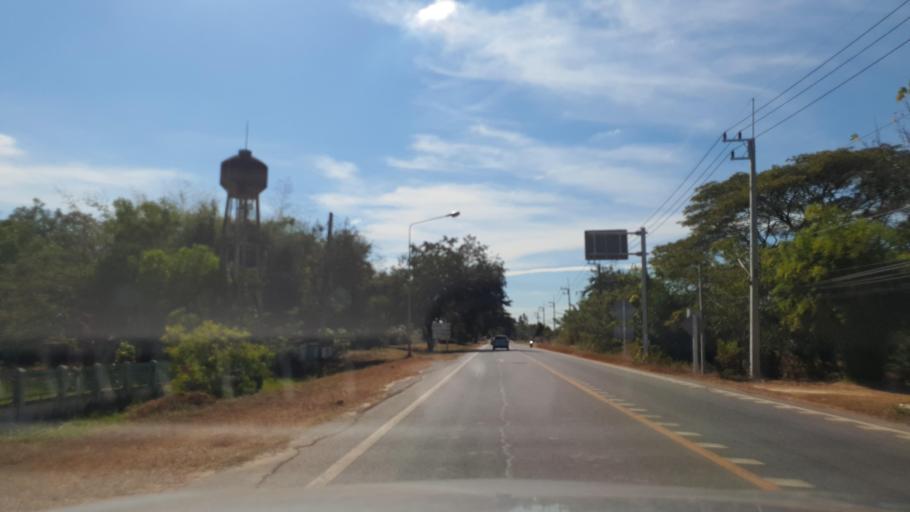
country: TH
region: Kalasin
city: Khao Wong
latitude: 16.7328
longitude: 104.0947
